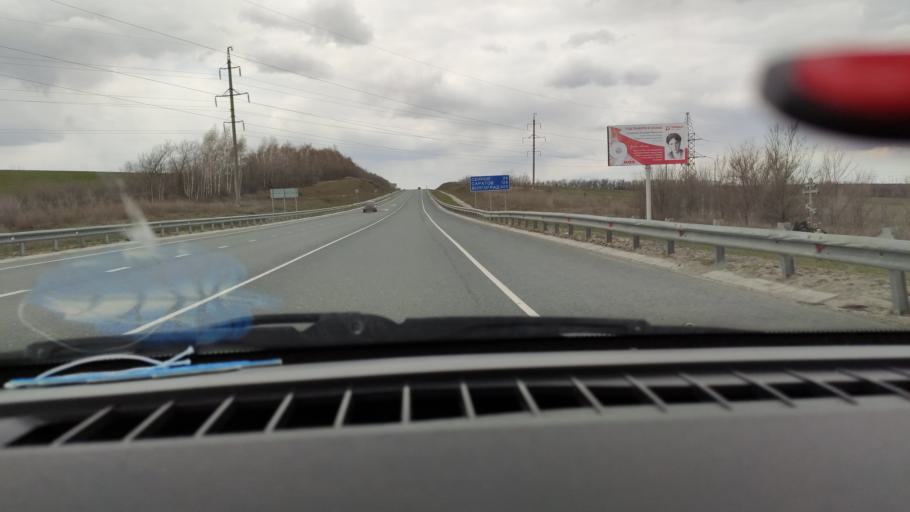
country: RU
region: Saratov
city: Shikhany
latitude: 52.1168
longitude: 47.2885
